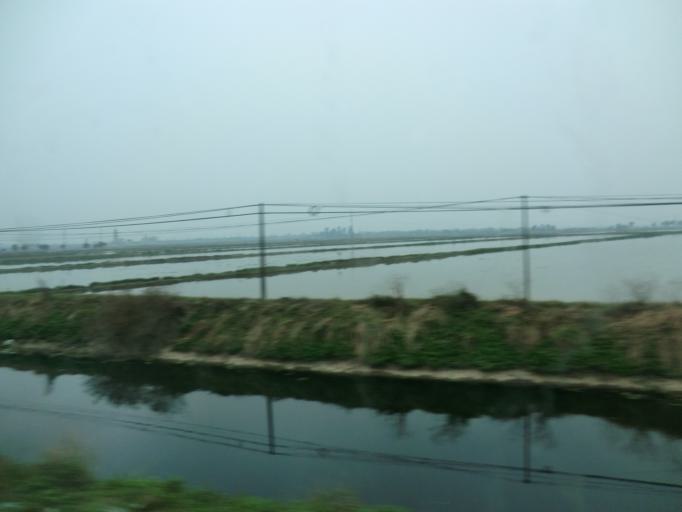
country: VN
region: Nam Dinh
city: Thi Tran Lam
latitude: 20.2939
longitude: 106.0231
